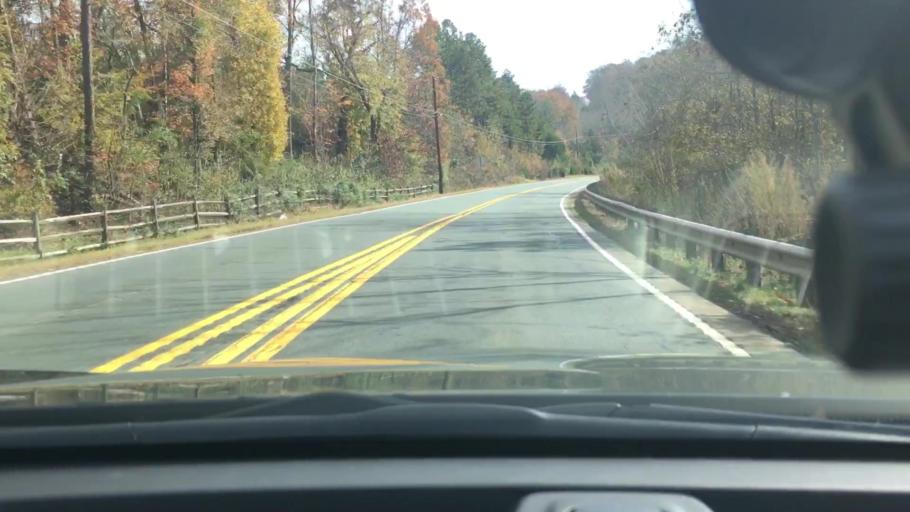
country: US
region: North Carolina
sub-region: Stanly County
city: Badin
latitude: 35.3133
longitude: -80.0926
